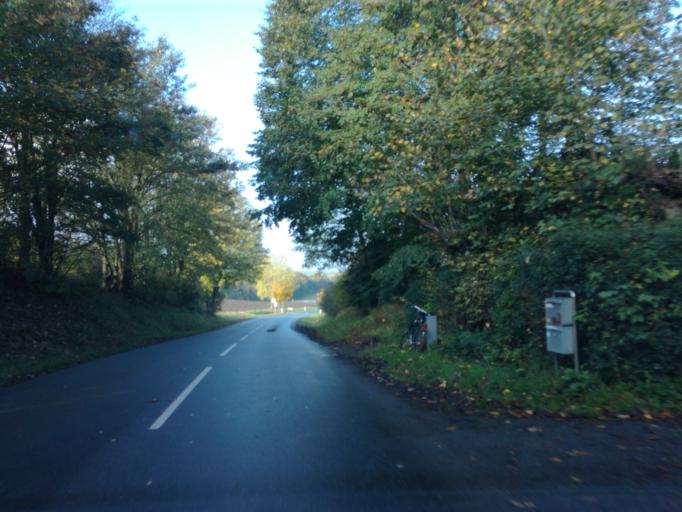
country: DK
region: South Denmark
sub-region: Vejle Kommune
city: Borkop
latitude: 55.6536
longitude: 9.6445
